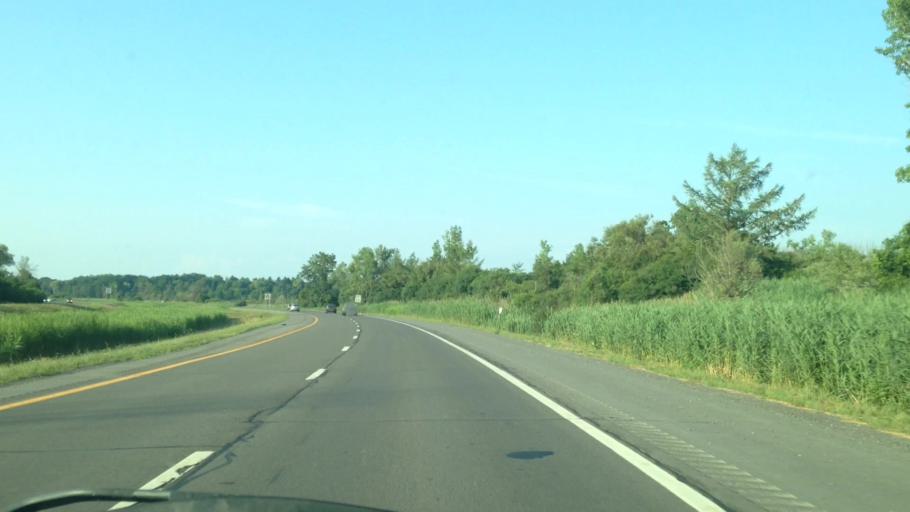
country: US
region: New York
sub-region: Onondaga County
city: East Syracuse
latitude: 43.0174
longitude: -76.0651
